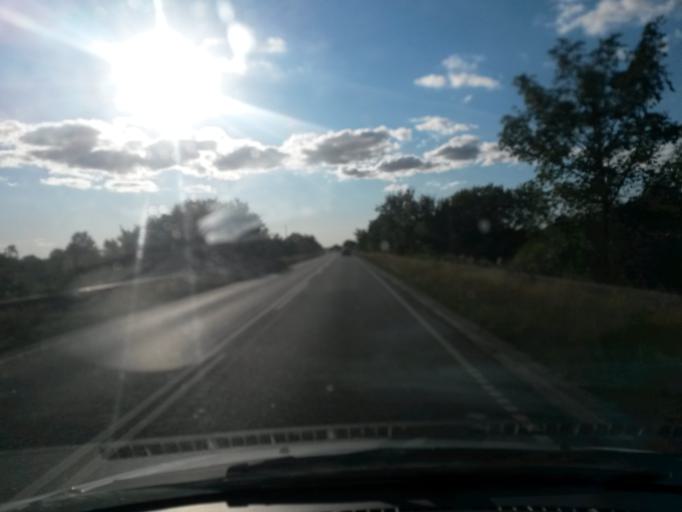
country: DK
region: Central Jutland
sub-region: Silkeborg Kommune
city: Kjellerup
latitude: 56.3001
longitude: 9.3613
